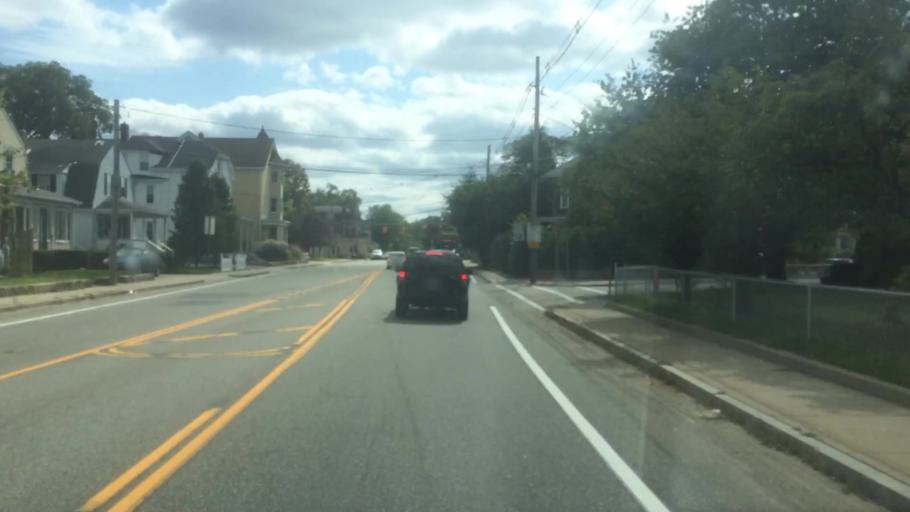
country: US
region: Rhode Island
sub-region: Providence County
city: Cranston
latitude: 41.7750
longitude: -71.4026
